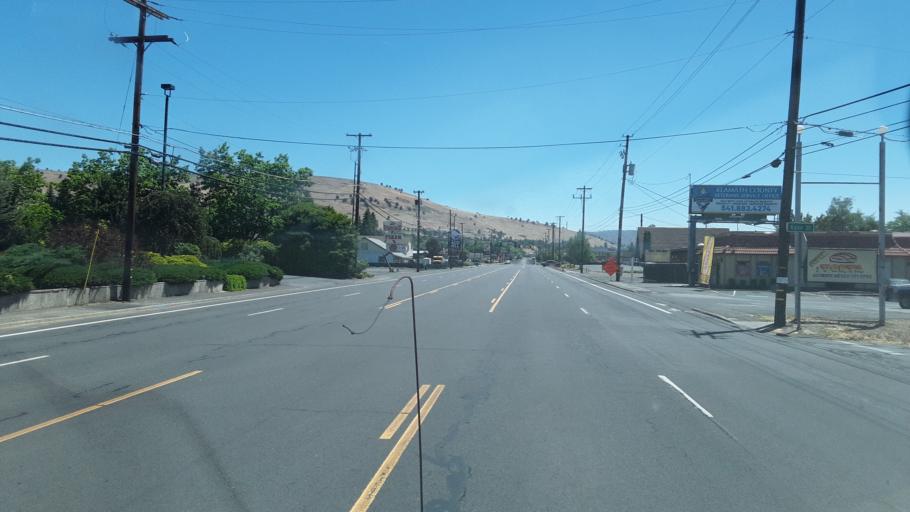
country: US
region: Oregon
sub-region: Klamath County
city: Altamont
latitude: 42.2065
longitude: -121.7254
